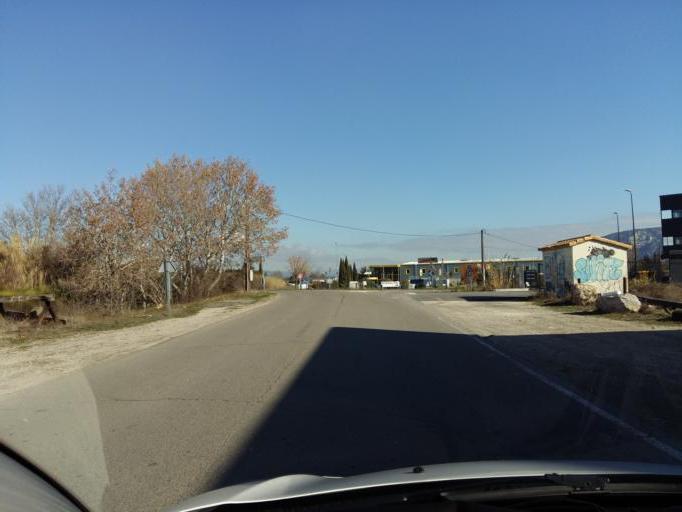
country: FR
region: Provence-Alpes-Cote d'Azur
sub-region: Departement du Vaucluse
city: Cavaillon
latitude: 43.8325
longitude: 5.0608
